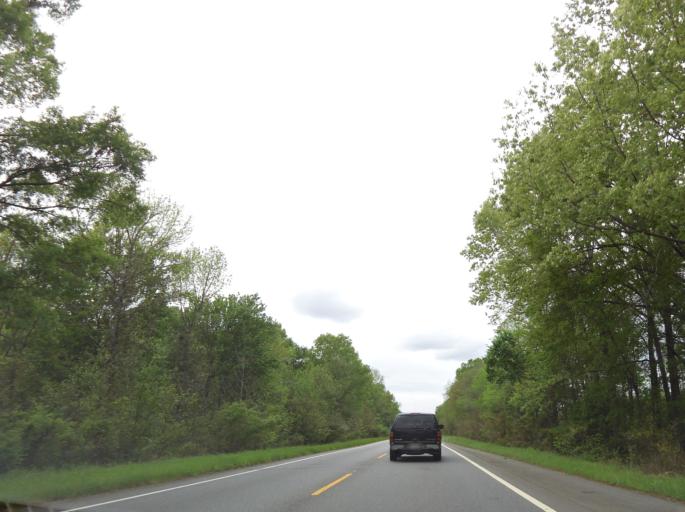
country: US
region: Georgia
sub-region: Houston County
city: Robins Air Force Base
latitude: 32.5422
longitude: -83.5223
